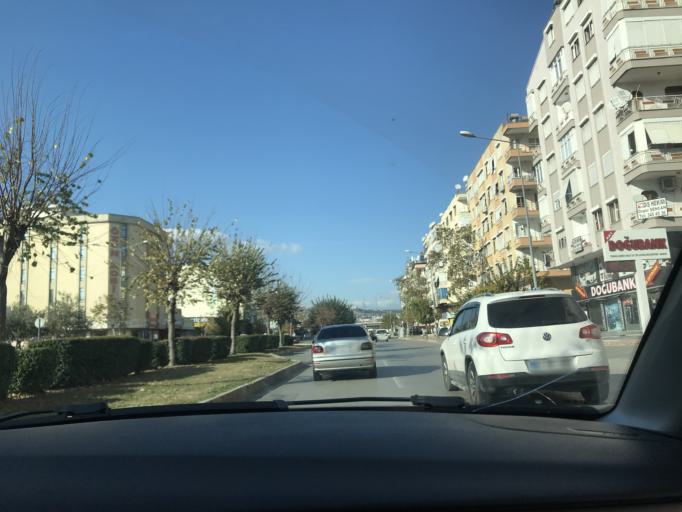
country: TR
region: Antalya
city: Antalya
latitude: 36.9080
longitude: 30.6993
